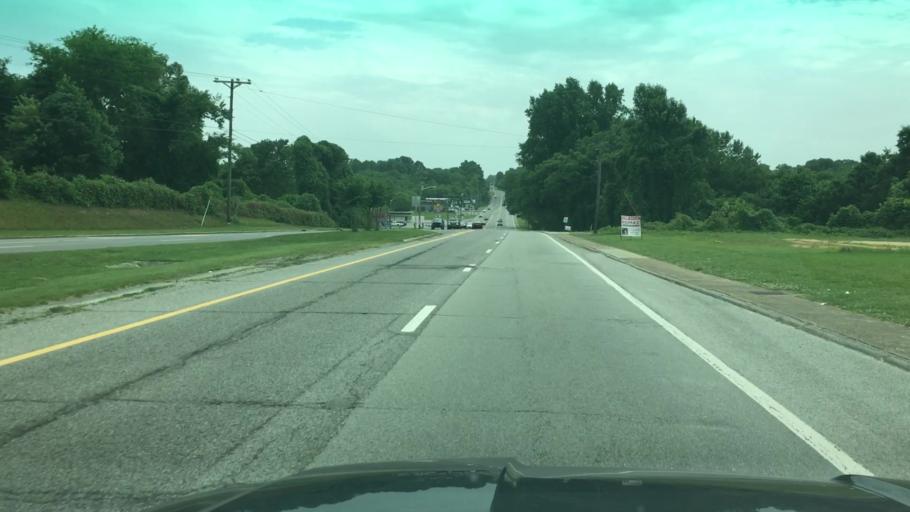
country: US
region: Tennessee
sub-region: Coffee County
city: Manchester
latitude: 35.4860
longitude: -86.0764
